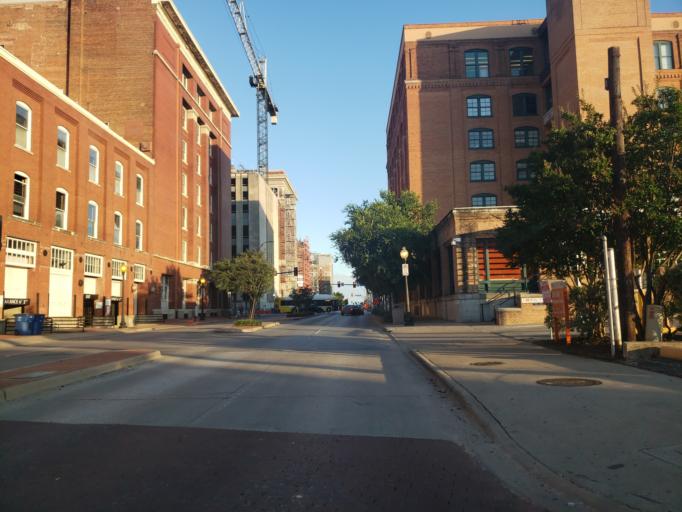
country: US
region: Texas
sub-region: Dallas County
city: Dallas
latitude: 32.7805
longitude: -96.8084
